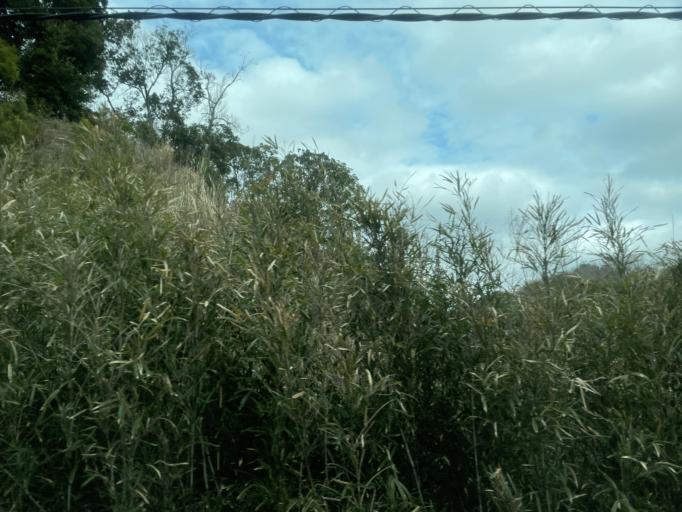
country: JP
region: Chiba
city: Narita
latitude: 35.8009
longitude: 140.2910
